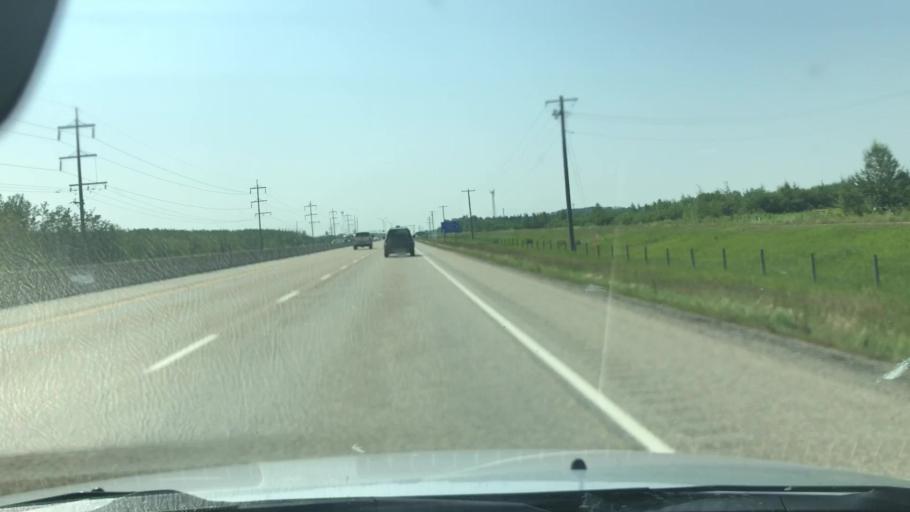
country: CA
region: Alberta
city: Devon
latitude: 53.4601
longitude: -113.7636
